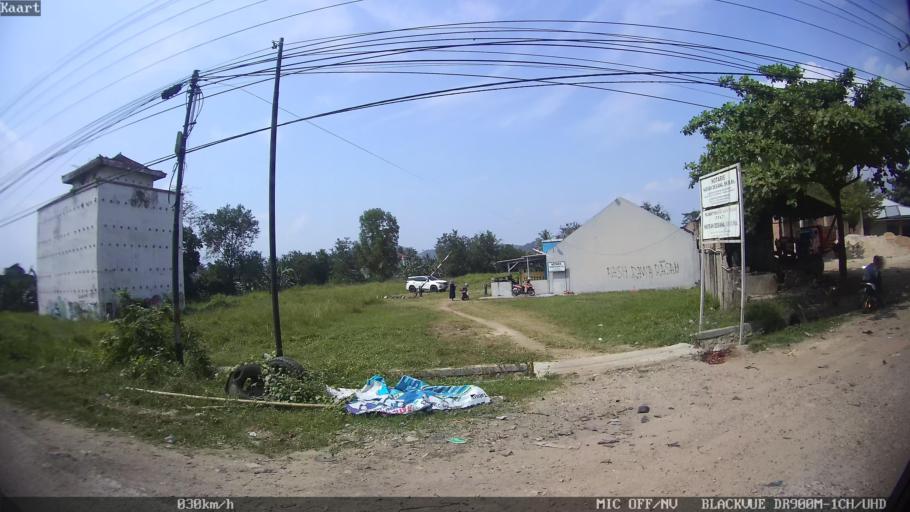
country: ID
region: Lampung
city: Pringsewu
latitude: -5.3627
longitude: 105.0012
